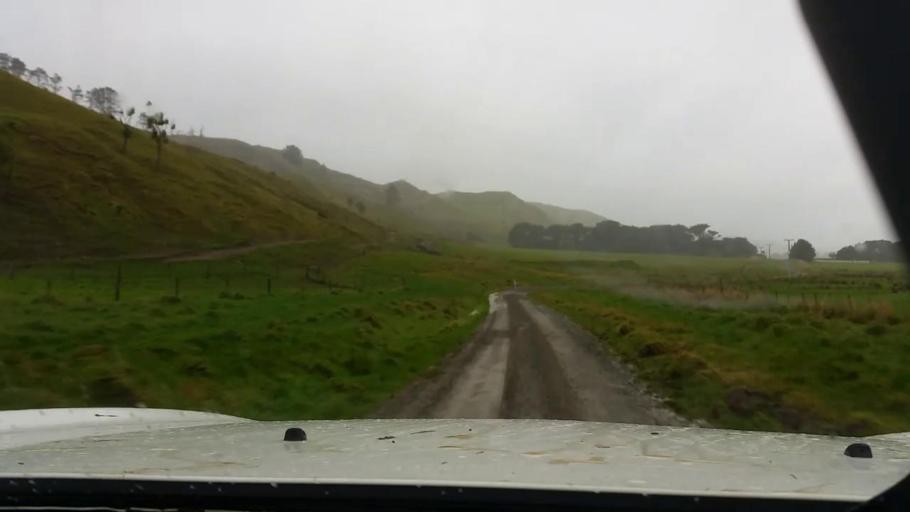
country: NZ
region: Wellington
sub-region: Masterton District
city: Masterton
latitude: -41.2602
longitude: 175.8974
